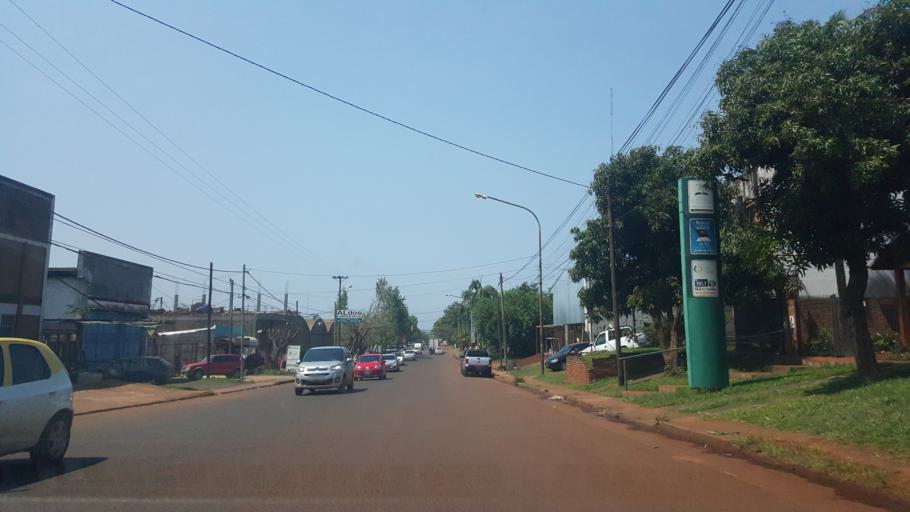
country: AR
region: Misiones
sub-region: Departamento de Capital
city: Posadas
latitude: -27.3862
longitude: -55.9134
